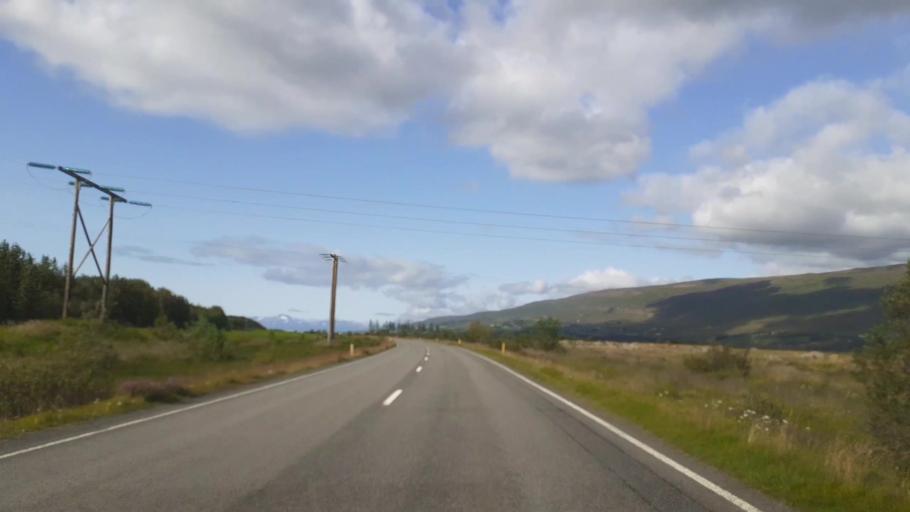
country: IS
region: Northeast
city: Akureyri
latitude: 65.6307
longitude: -18.0697
